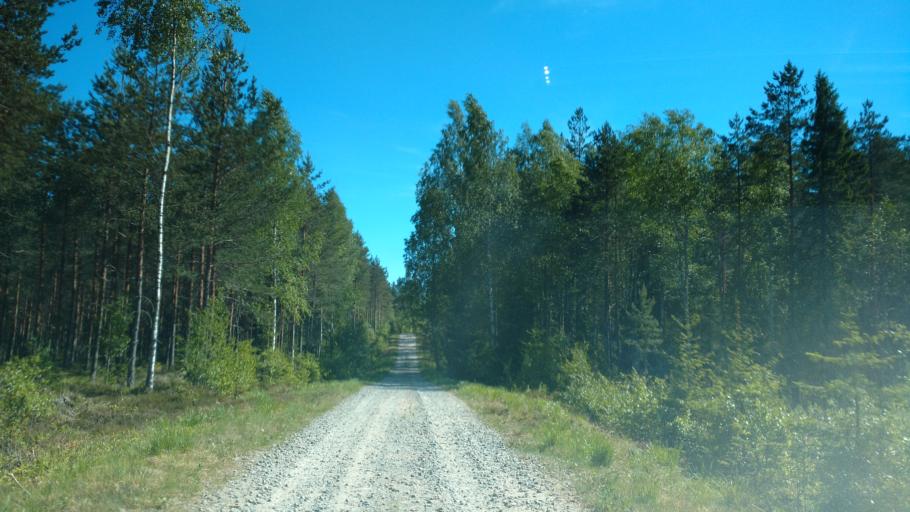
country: FI
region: Varsinais-Suomi
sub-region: Salo
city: Halikko
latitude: 60.4374
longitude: 22.9709
